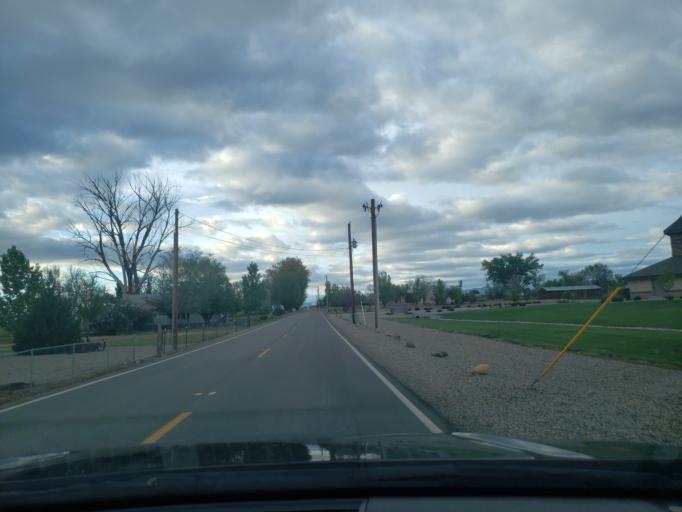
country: US
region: Colorado
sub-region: Mesa County
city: Fruita
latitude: 39.1790
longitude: -108.7290
